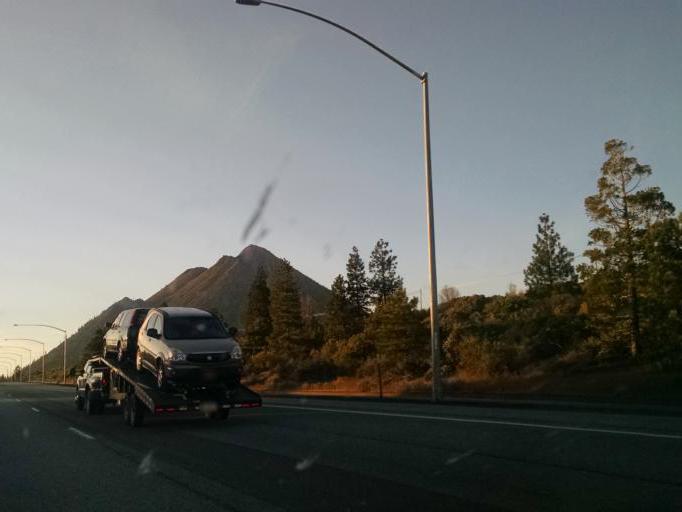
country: US
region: California
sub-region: Siskiyou County
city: Mount Shasta
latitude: 41.3341
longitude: -122.3338
